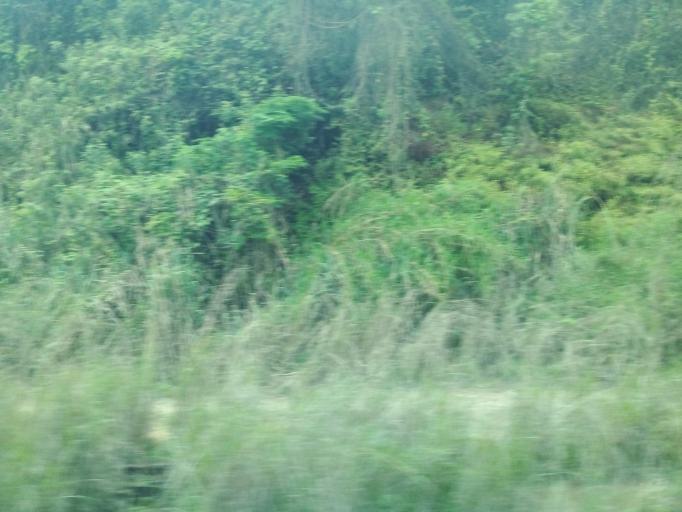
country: BR
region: Minas Gerais
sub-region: Nova Era
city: Nova Era
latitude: -19.7311
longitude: -42.9836
